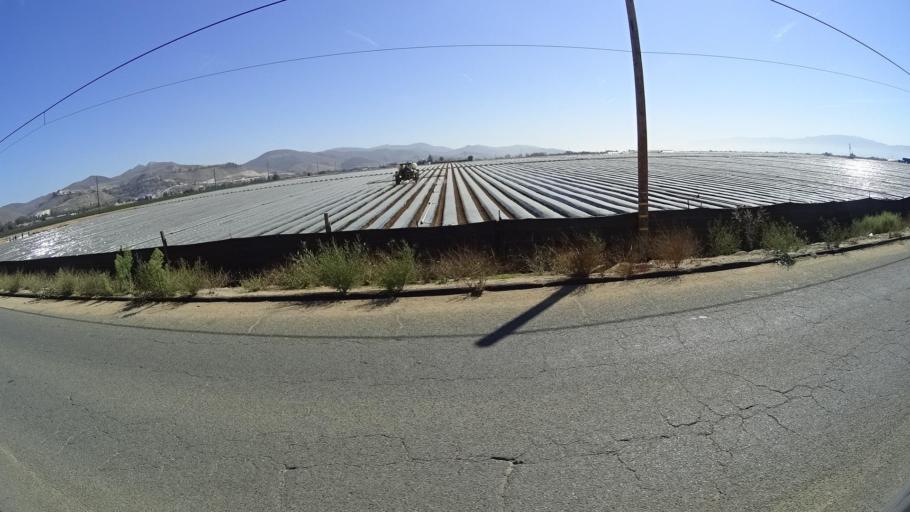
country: US
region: California
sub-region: Monterey County
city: Prunedale
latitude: 36.7470
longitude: -121.6297
